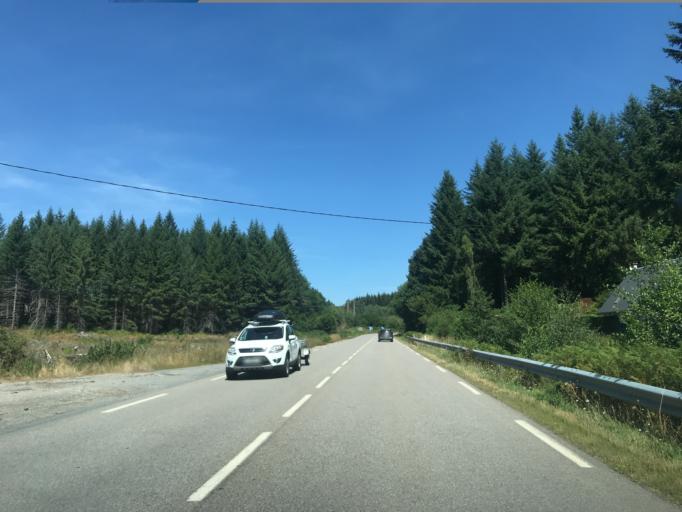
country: FR
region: Limousin
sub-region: Departement de la Correze
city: Egletons
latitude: 45.4523
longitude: 2.1121
